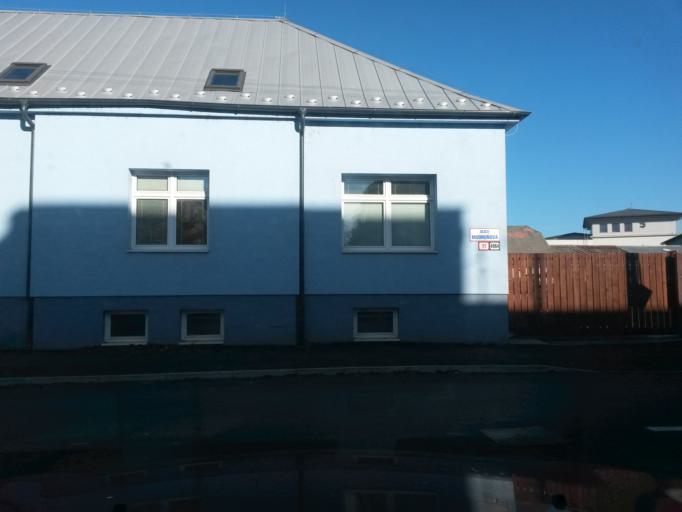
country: SK
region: Presovsky
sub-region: Okres Presov
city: Presov
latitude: 49.0030
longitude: 21.2343
